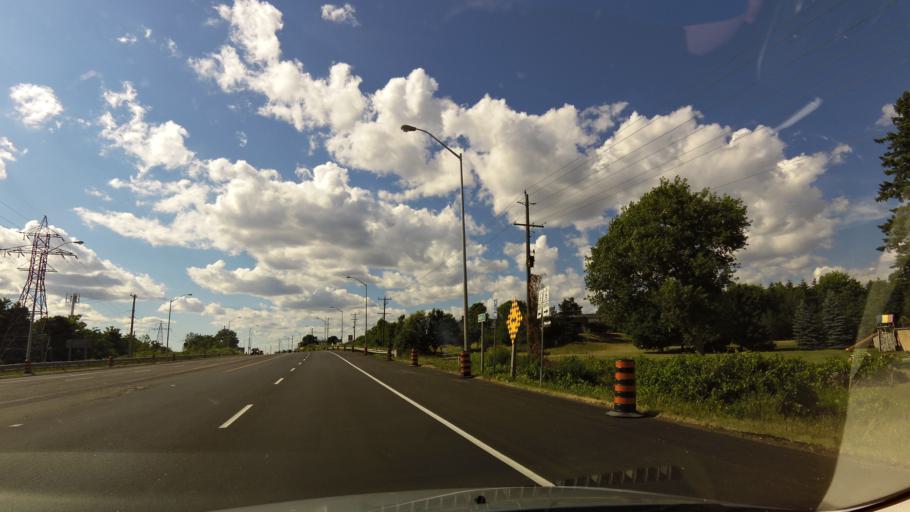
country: CA
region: Ontario
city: Ancaster
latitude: 43.3970
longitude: -80.0319
